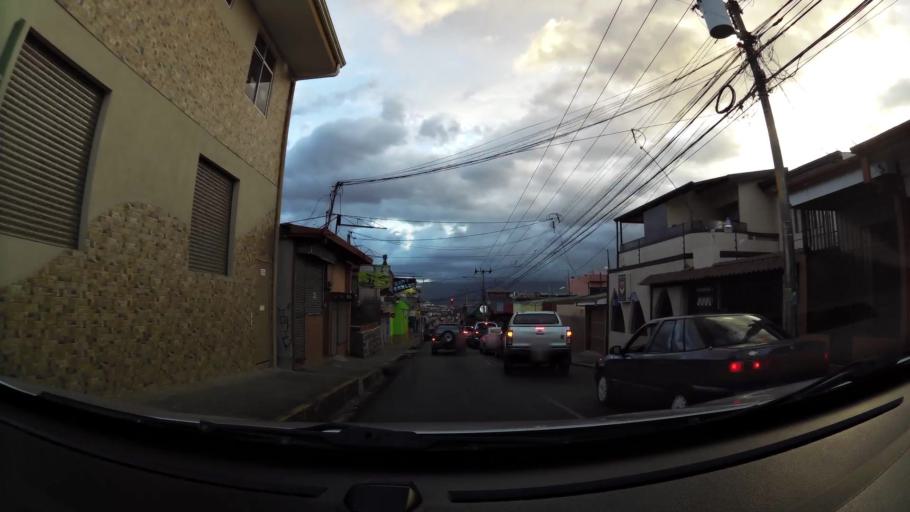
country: CR
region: Heredia
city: Heredia
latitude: 9.9992
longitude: -84.1133
